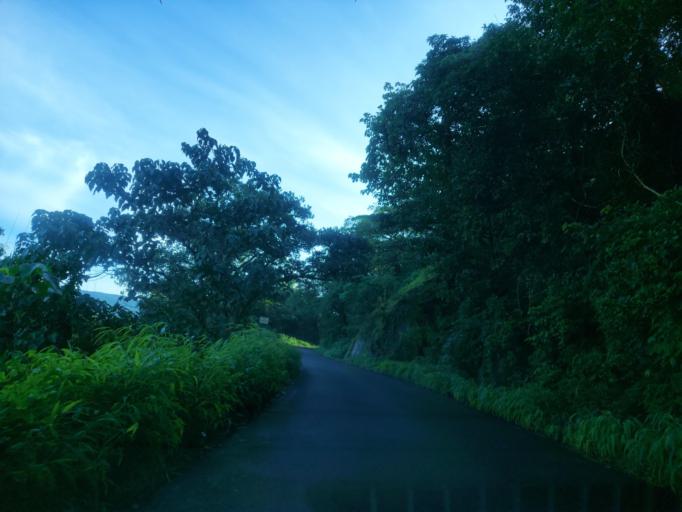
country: IN
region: Maharashtra
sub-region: Sindhudurg
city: Savantvadi
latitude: 15.9367
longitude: 73.9699
